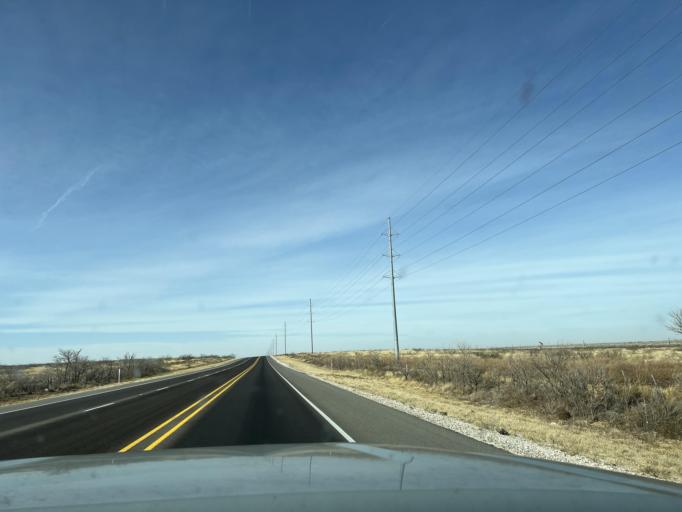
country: US
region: Texas
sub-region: Andrews County
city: Andrews
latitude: 32.3525
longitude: -102.7443
